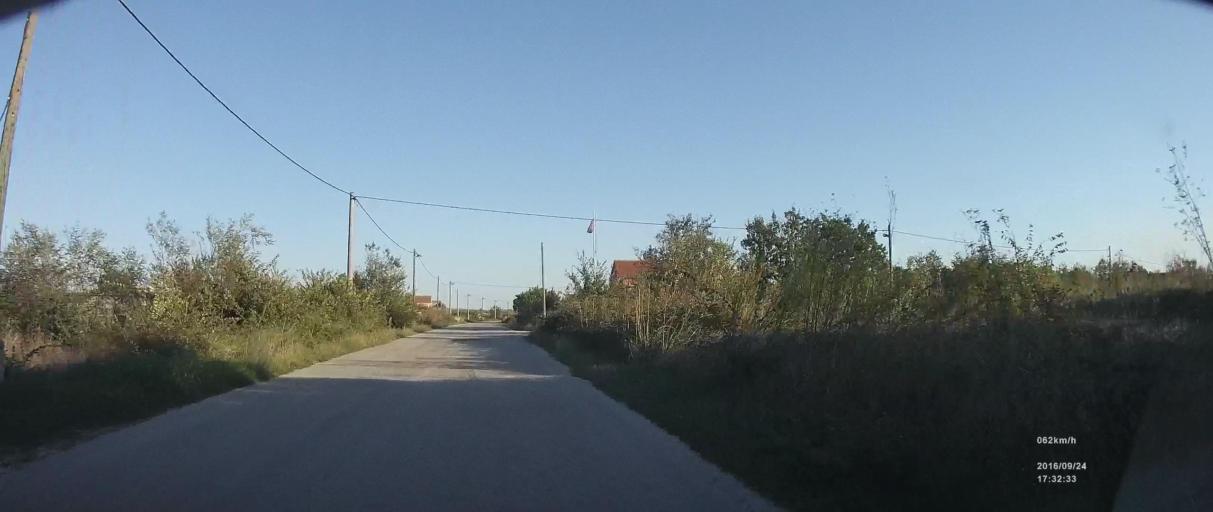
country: HR
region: Zadarska
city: Posedarje
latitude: 44.1814
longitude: 15.4511
